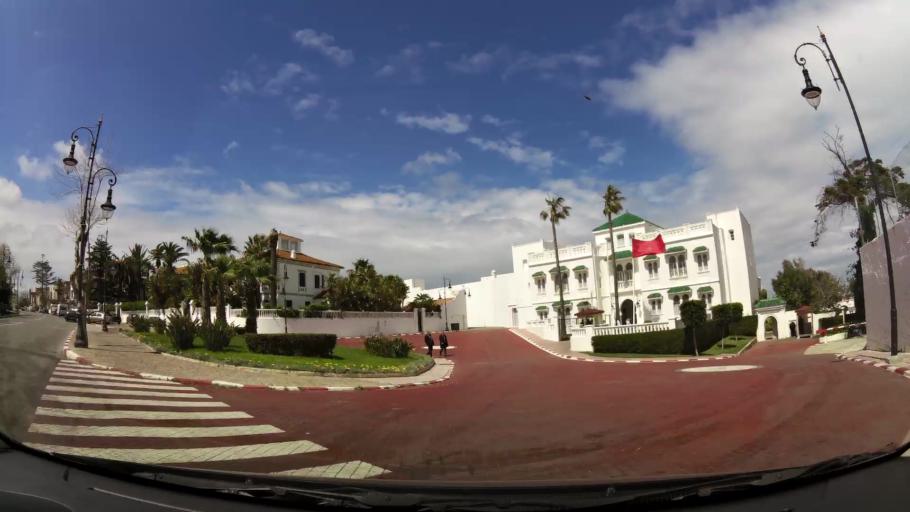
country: MA
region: Tanger-Tetouan
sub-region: Tanger-Assilah
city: Tangier
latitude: 35.7909
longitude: -5.8249
